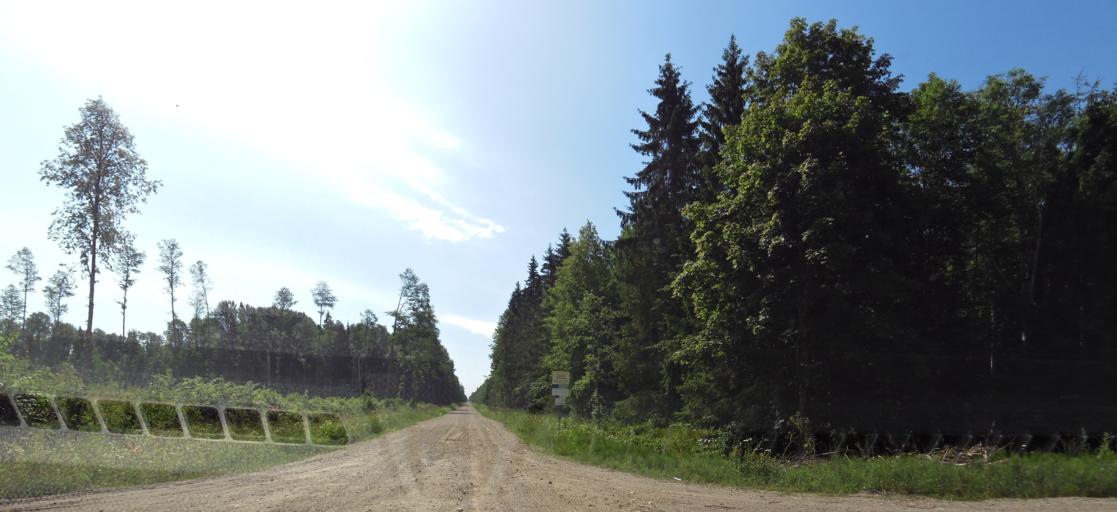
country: LT
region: Panevezys
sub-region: Birzai
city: Birzai
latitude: 56.2433
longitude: 24.9797
